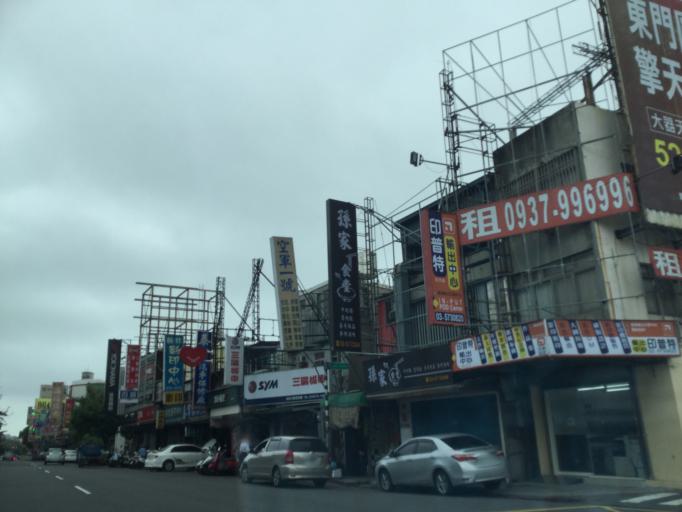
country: TW
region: Taiwan
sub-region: Hsinchu
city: Hsinchu
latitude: 24.7912
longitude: 121.0045
